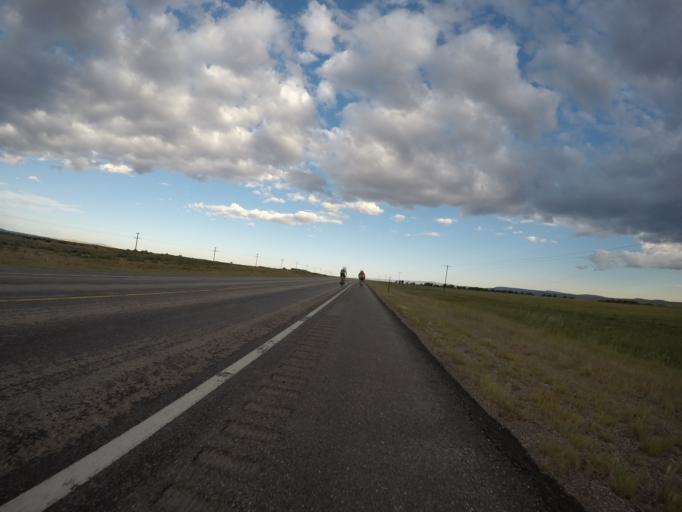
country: US
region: Wyoming
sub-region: Carbon County
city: Saratoga
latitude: 41.8884
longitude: -106.1662
